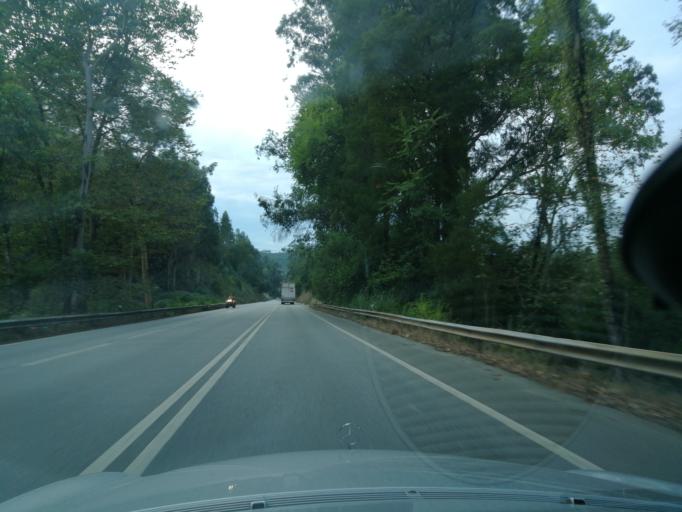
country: PT
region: Aveiro
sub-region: Agueda
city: Valongo
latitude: 40.6286
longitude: -8.4655
